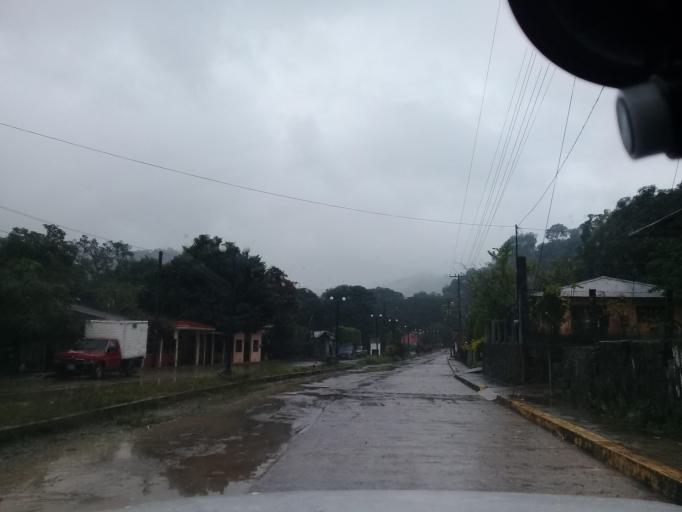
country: MX
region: Veracruz
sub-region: Chalma
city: San Pedro Coyutla
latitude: 21.2350
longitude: -98.4605
